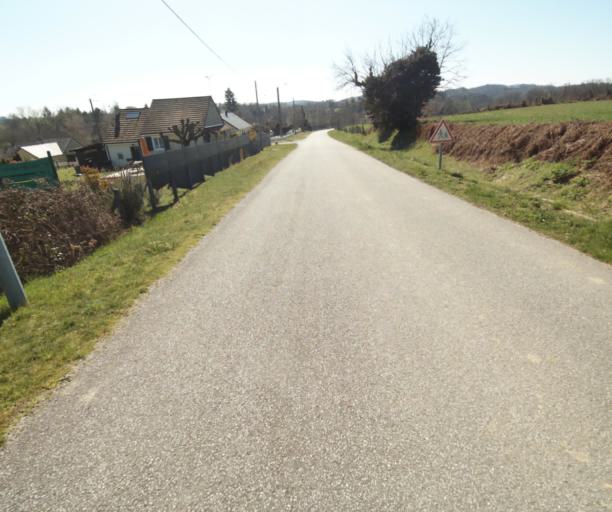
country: FR
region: Limousin
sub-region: Departement de la Correze
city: Saint-Mexant
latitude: 45.3124
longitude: 1.6471
